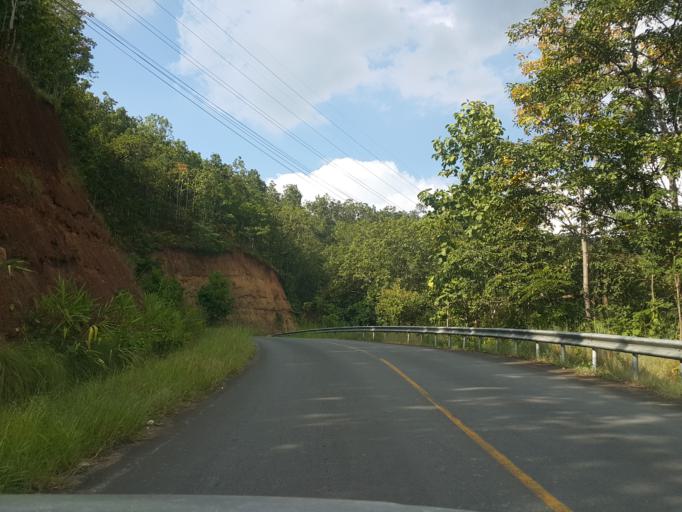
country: TH
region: Chiang Mai
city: Mae Chaem
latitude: 18.5393
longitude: 98.3736
